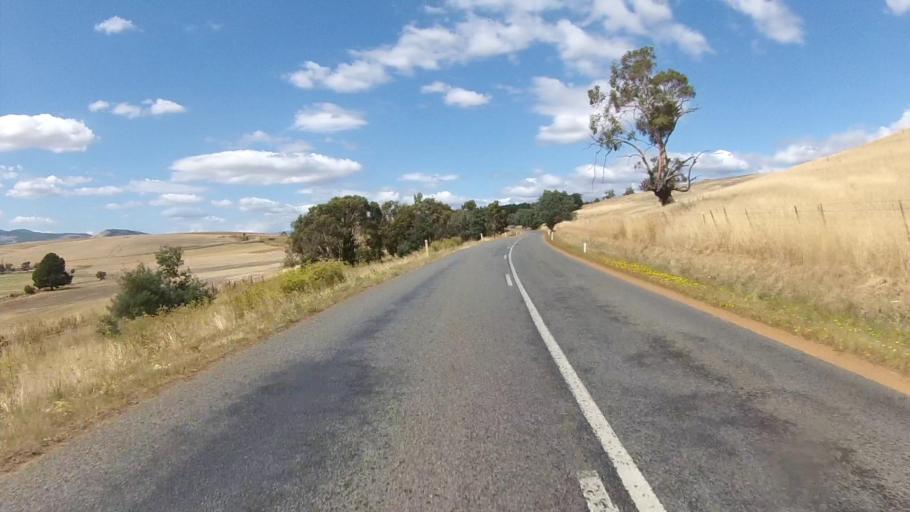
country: AU
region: Tasmania
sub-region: Derwent Valley
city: New Norfolk
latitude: -42.6852
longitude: 146.8692
